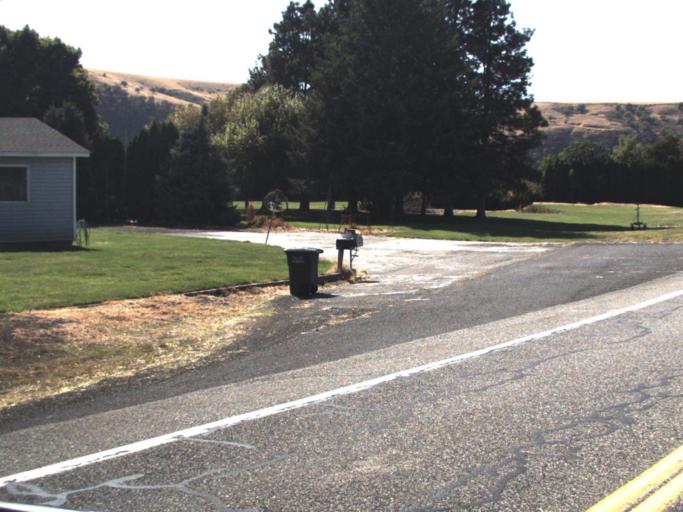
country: US
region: Washington
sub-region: Walla Walla County
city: Waitsburg
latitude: 46.2699
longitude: -118.1653
